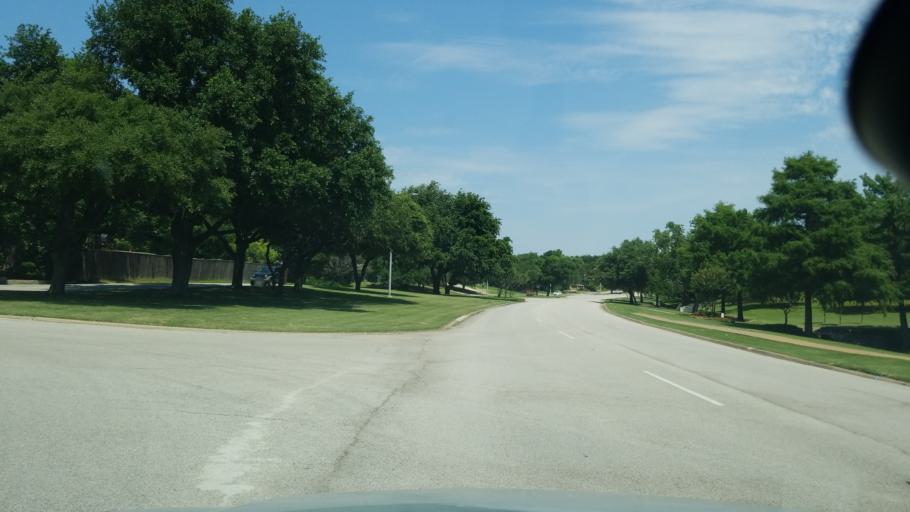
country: US
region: Texas
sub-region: Dallas County
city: Irving
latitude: 32.8474
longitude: -96.9378
